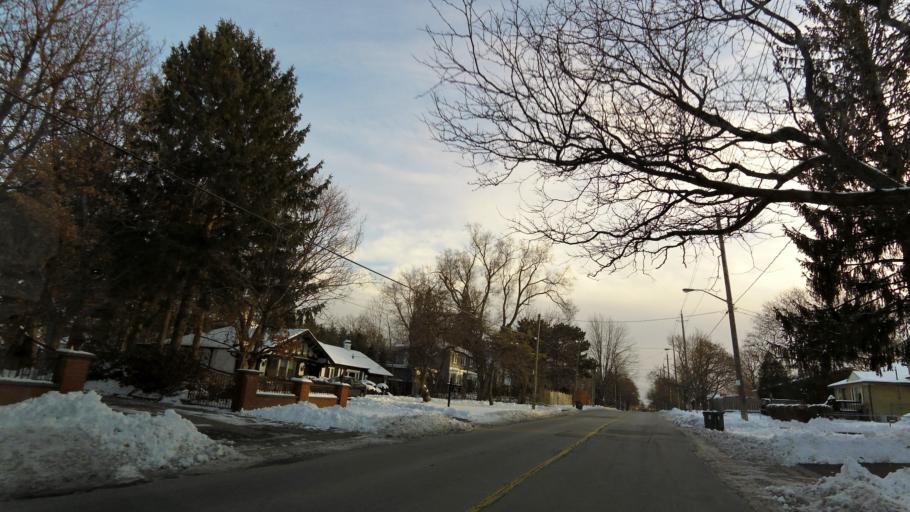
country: CA
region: Ontario
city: Etobicoke
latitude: 43.6520
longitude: -79.5504
